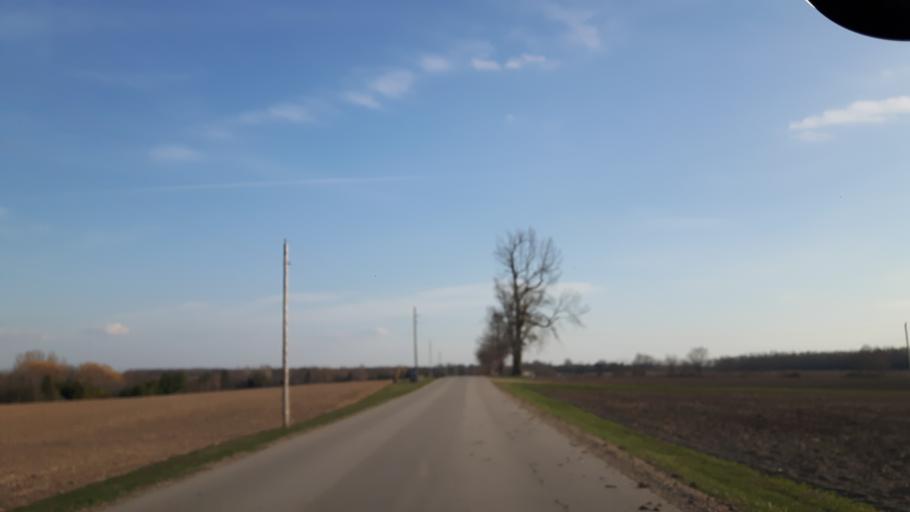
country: CA
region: Ontario
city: Goderich
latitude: 43.6903
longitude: -81.6645
